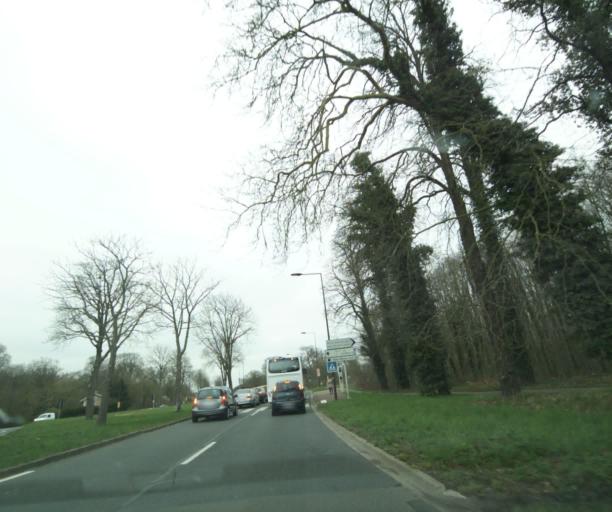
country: FR
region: Ile-de-France
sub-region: Departement des Yvelines
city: Saint-Germain-en-Laye
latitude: 48.9097
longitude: 2.0753
